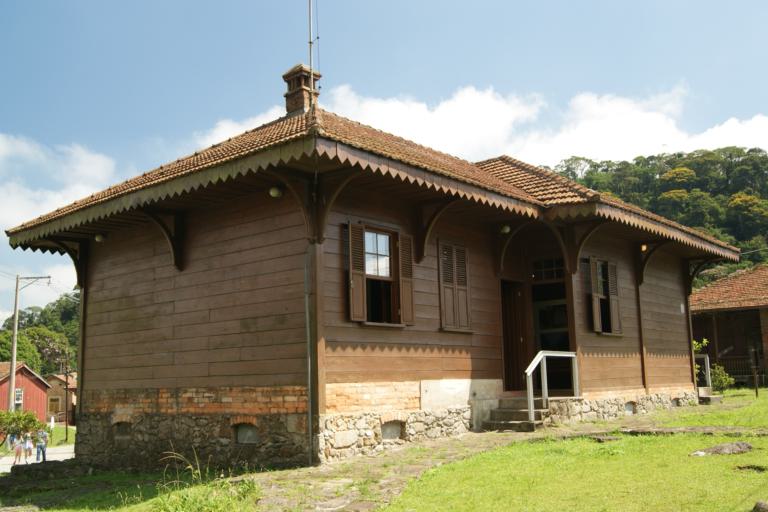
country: BR
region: Sao Paulo
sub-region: Rio Grande Da Serra
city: Rio Grande da Serra
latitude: -23.7768
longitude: -46.3011
